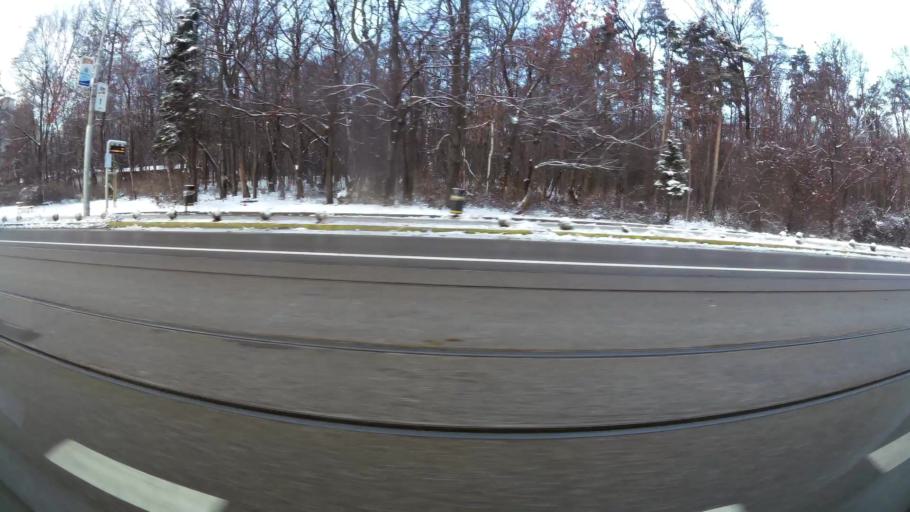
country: BG
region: Sofia-Capital
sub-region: Stolichna Obshtina
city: Sofia
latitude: 42.6654
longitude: 23.3176
